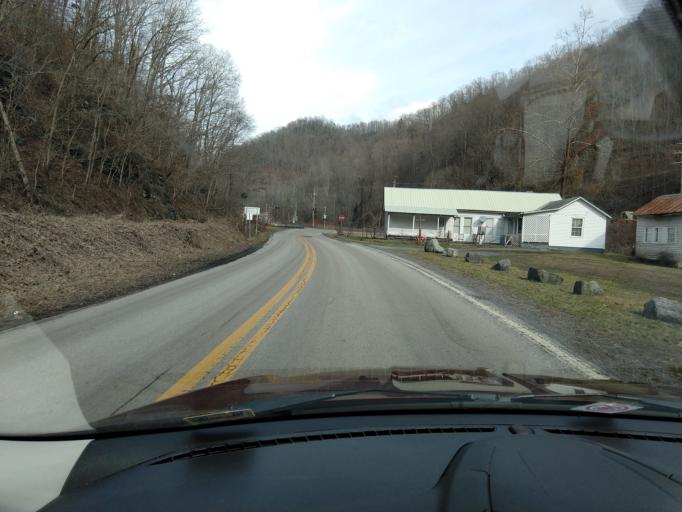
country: US
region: West Virginia
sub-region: McDowell County
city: Welch
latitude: 37.3218
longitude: -81.6911
